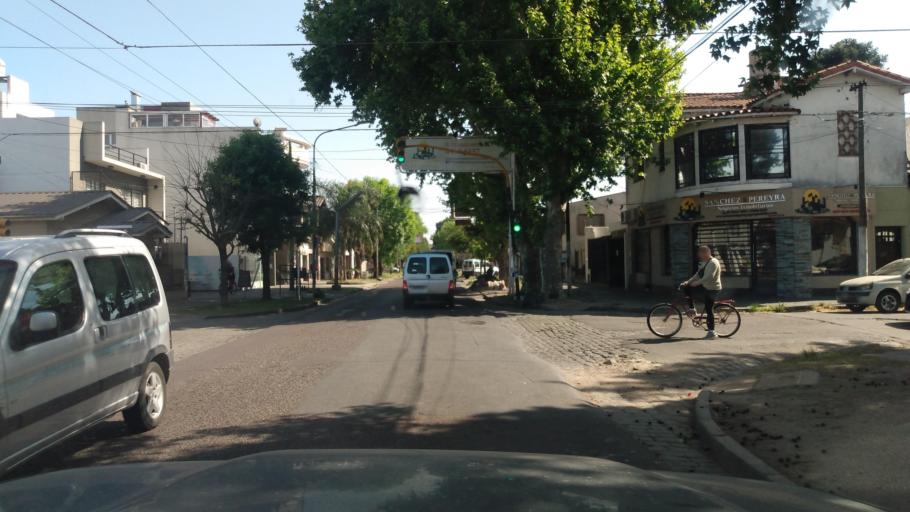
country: AR
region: Buenos Aires
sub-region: Partido de Moron
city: Moron
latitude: -34.6429
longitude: -58.5953
